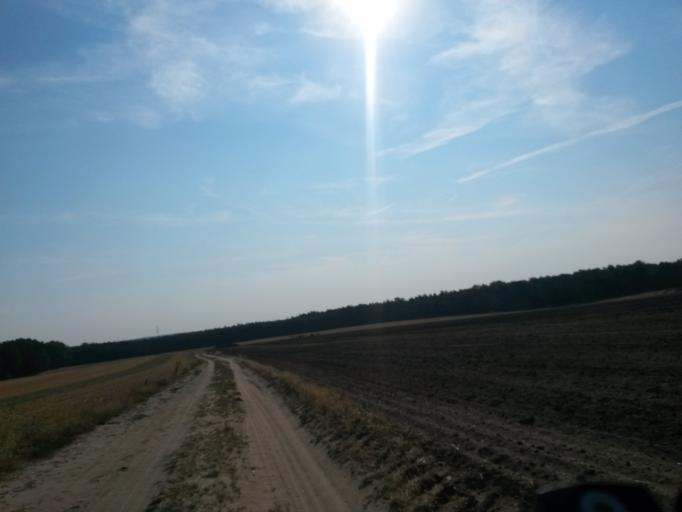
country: DE
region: Saxony-Anhalt
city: Nudersdorf
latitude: 51.9049
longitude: 12.5888
